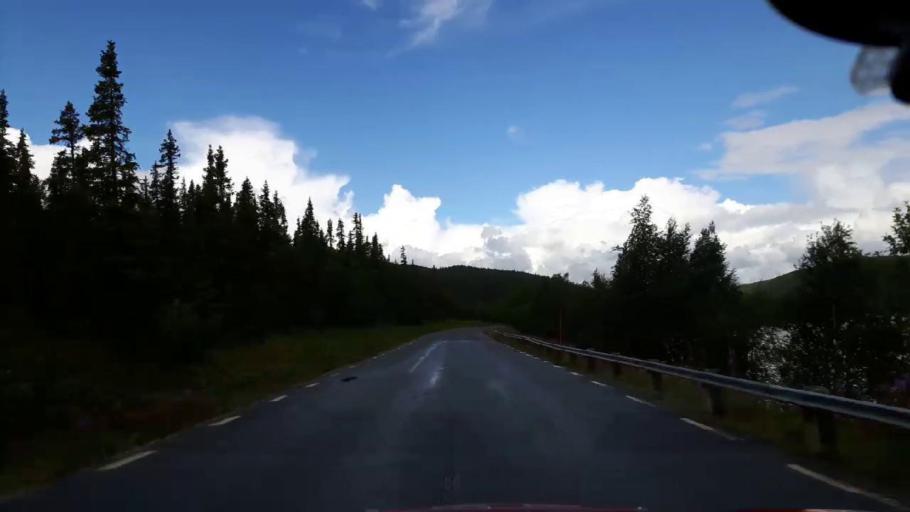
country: SE
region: Vaesterbotten
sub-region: Vilhelmina Kommun
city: Sjoberg
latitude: 65.0101
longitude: 15.1777
